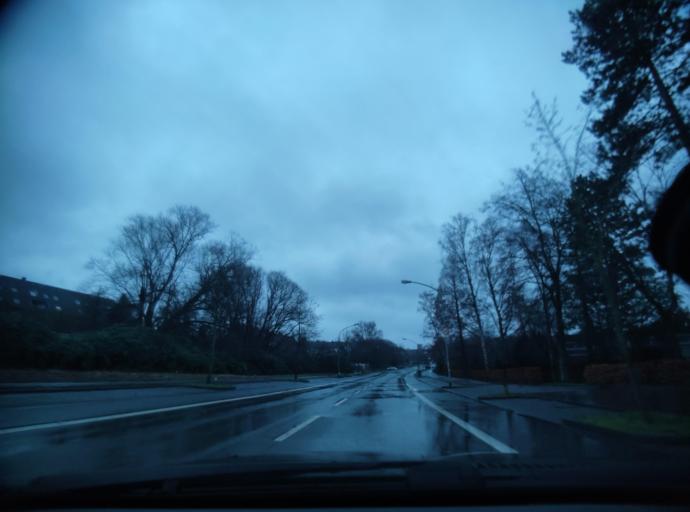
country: DE
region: North Rhine-Westphalia
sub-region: Regierungsbezirk Dusseldorf
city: Essen
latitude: 51.4820
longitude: 7.0348
